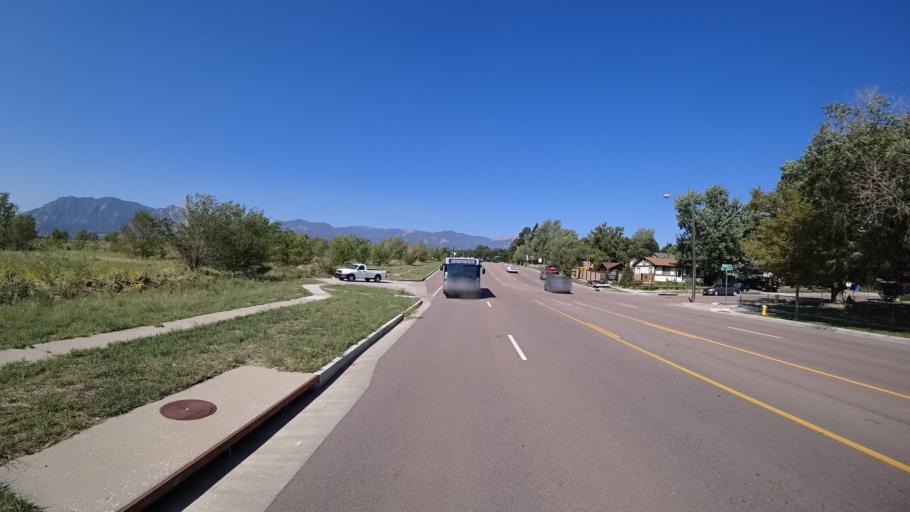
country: US
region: Colorado
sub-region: El Paso County
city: Colorado Springs
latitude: 38.8173
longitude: -104.7894
